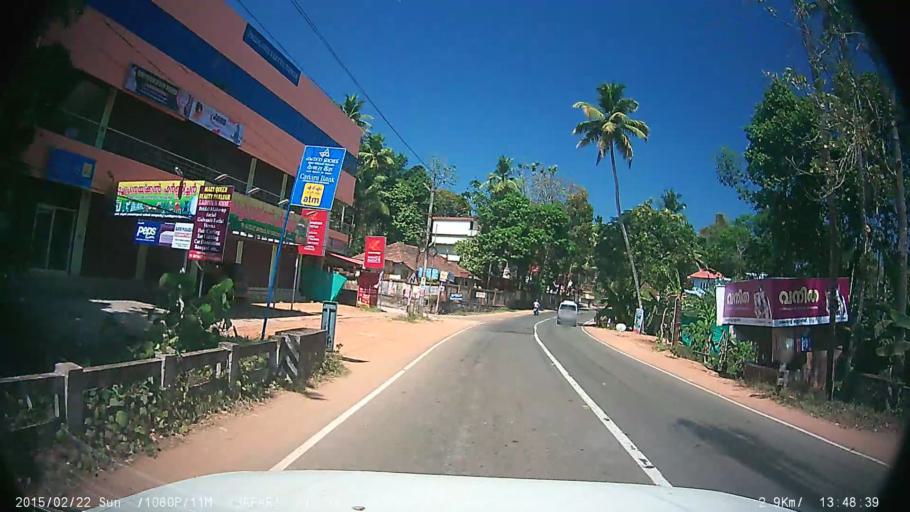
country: IN
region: Kerala
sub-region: Kottayam
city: Changanacheri
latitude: 9.4955
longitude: 76.6295
